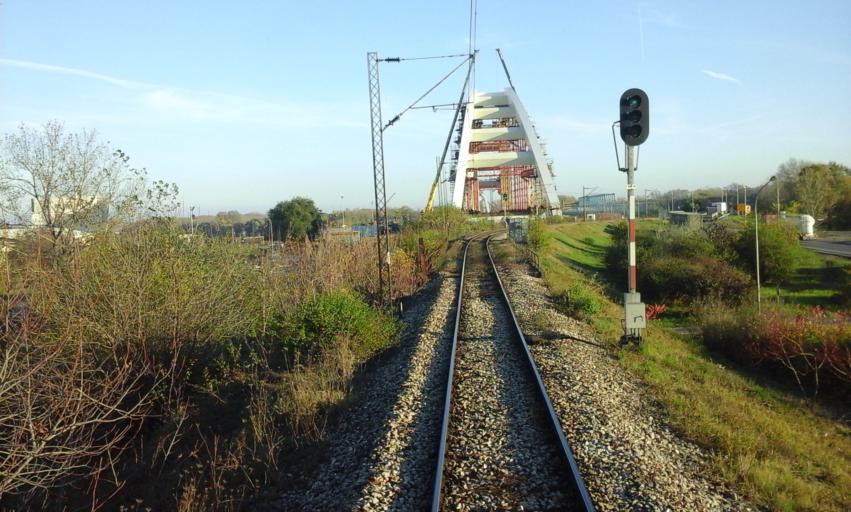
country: RS
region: Autonomna Pokrajina Vojvodina
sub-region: Juznobacki Okrug
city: Novi Sad
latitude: 45.2651
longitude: 19.8543
